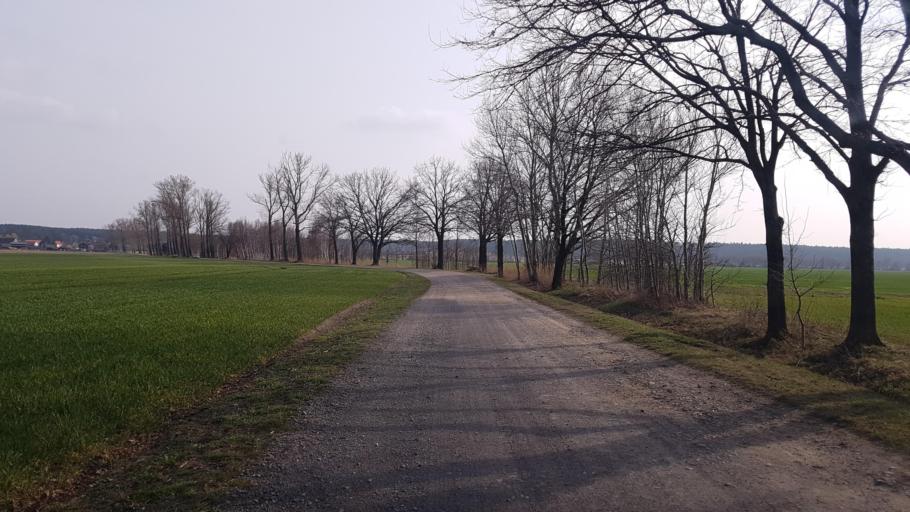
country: DE
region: Brandenburg
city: Merzdorf
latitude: 51.4131
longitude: 13.5267
